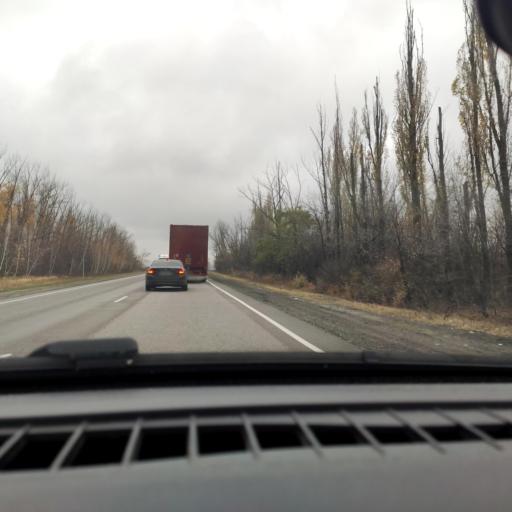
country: RU
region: Voronezj
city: Ostrogozhsk
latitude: 51.0171
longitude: 38.9848
